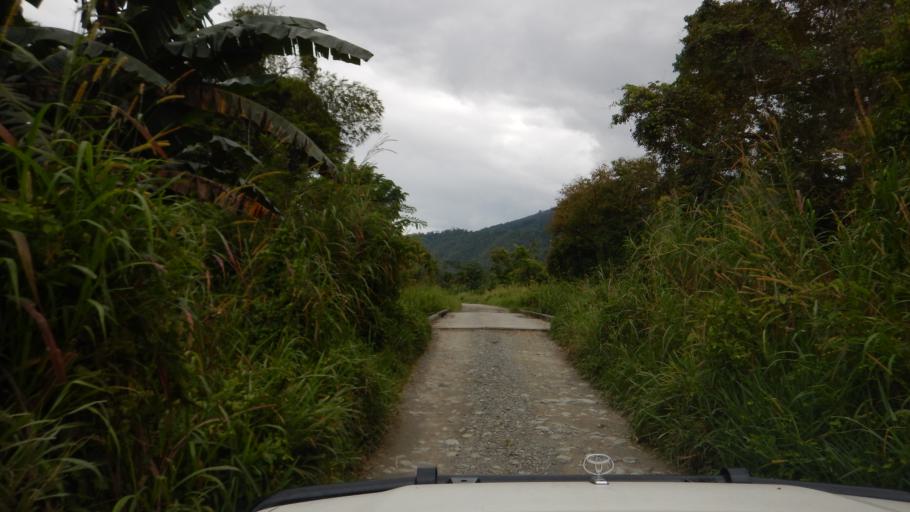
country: PG
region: Northern Province
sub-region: Sohe
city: Kokoda
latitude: -8.9190
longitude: 147.8664
